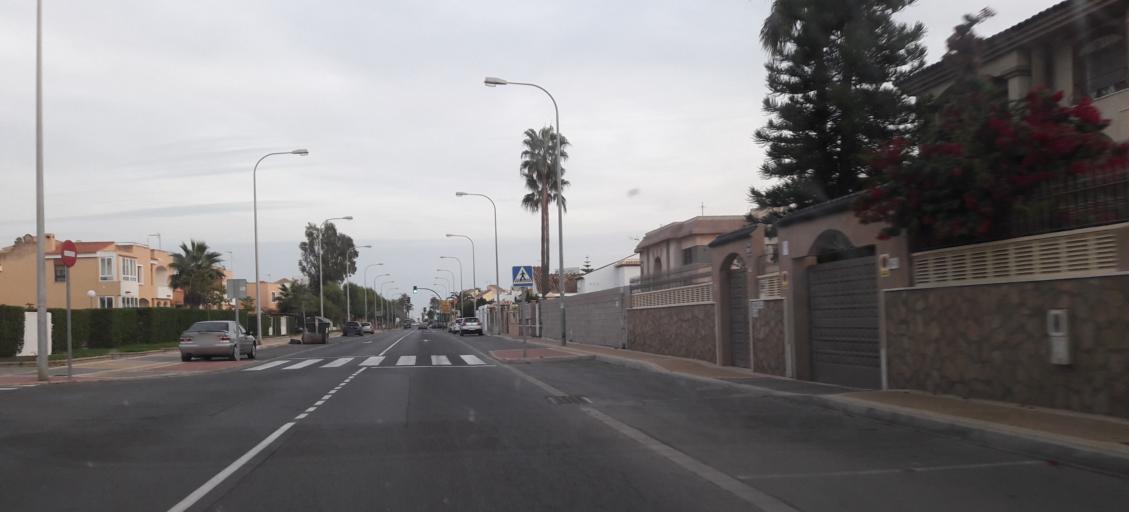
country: ES
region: Andalusia
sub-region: Provincia de Almeria
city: Roquetas de Mar
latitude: 36.7298
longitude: -2.6274
